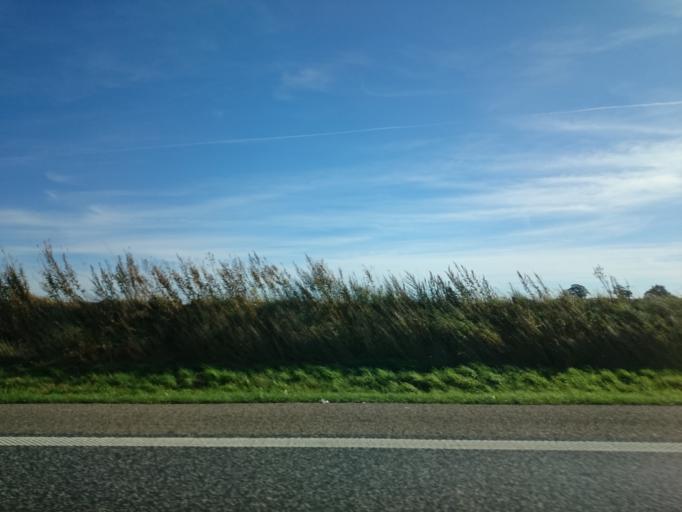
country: DK
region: Central Jutland
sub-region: Hedensted Kommune
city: Hedensted
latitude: 55.8507
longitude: 9.7448
